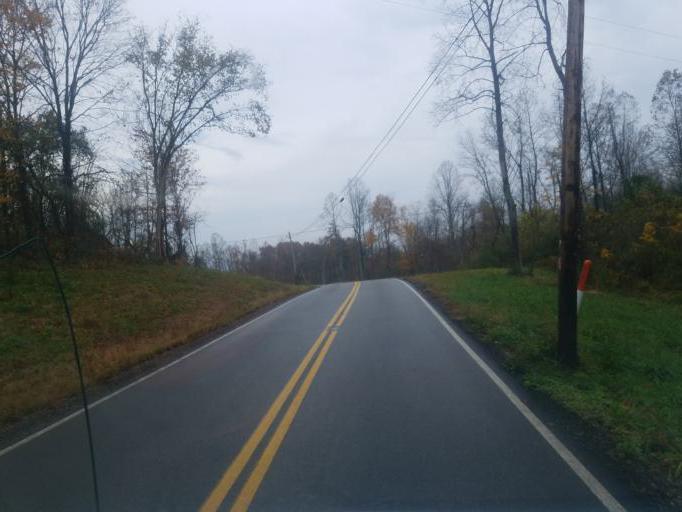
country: US
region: Ohio
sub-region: Morgan County
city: McConnelsville
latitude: 39.5663
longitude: -81.7838
